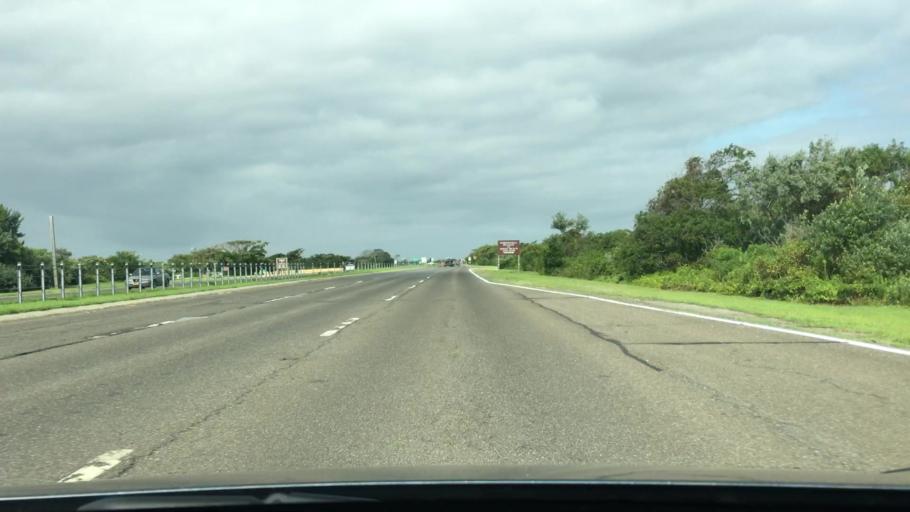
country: US
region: New York
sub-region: Nassau County
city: Point Lookout
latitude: 40.5954
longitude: -73.5193
